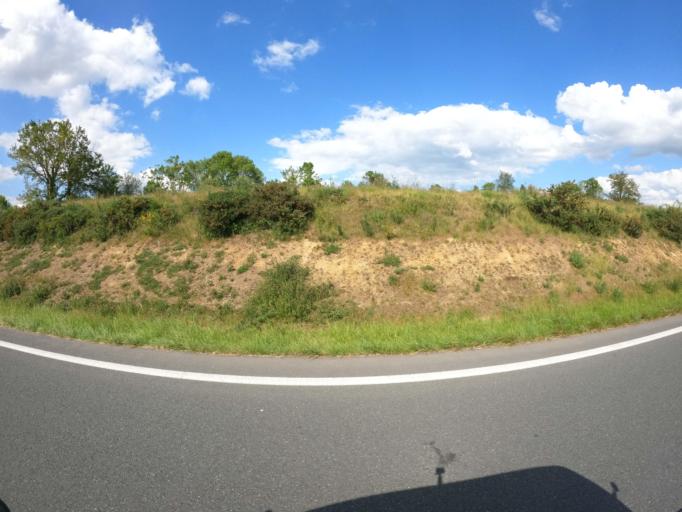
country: FR
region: Pays de la Loire
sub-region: Departement de Maine-et-Loire
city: La Tessoualle
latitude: 47.0250
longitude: -0.8855
